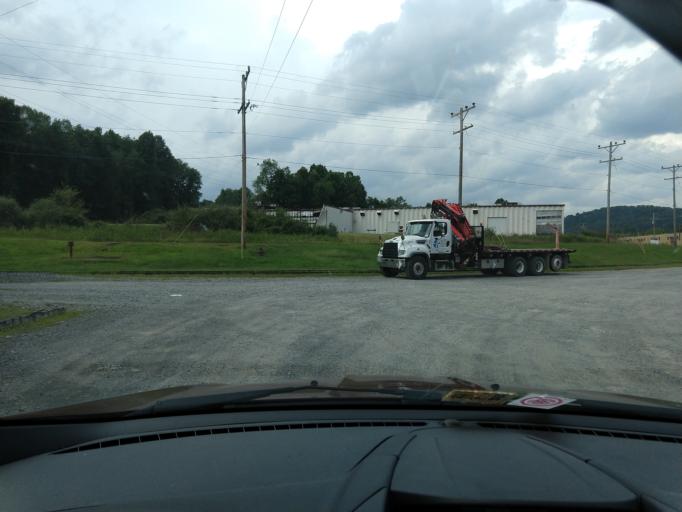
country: US
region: West Virginia
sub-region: Harrison County
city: Clarksburg
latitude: 39.2626
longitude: -80.3626
